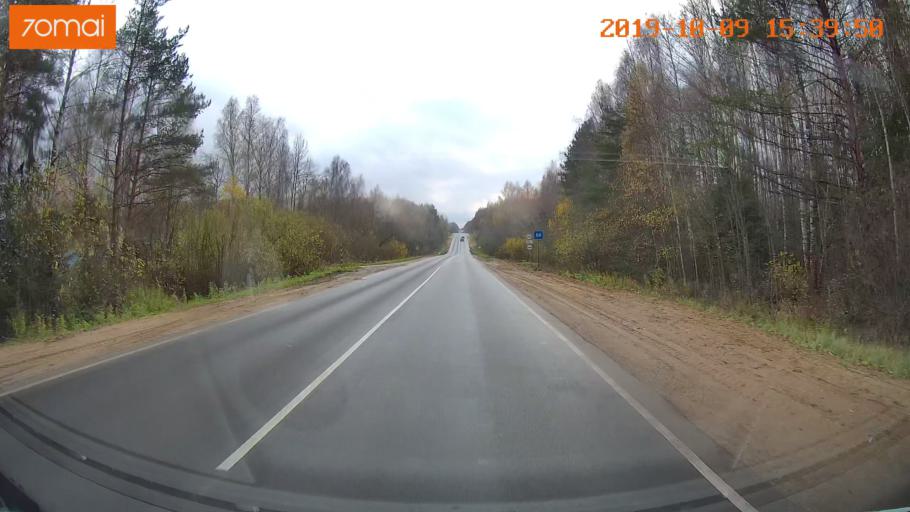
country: RU
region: Kostroma
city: Oktyabr'skiy
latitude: 57.8933
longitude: 41.1566
